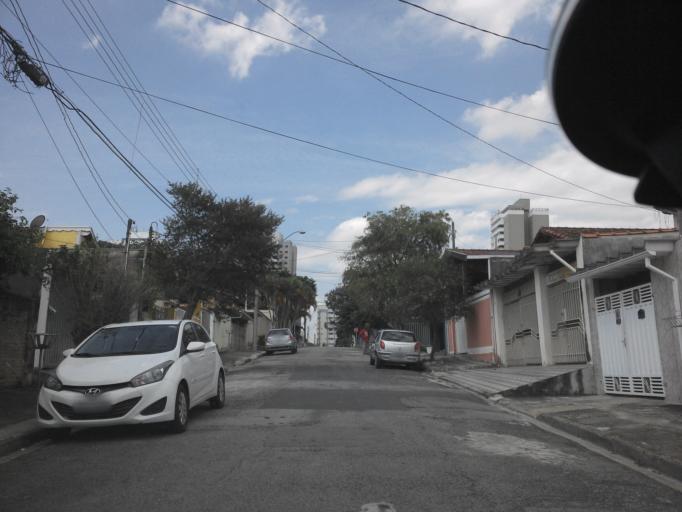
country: BR
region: Sao Paulo
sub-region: Taubate
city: Taubate
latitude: -23.0375
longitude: -45.5708
